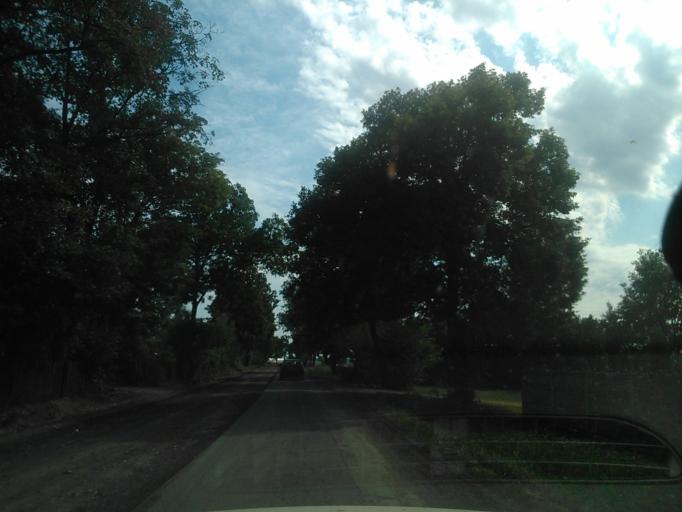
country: PL
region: Warmian-Masurian Voivodeship
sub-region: Powiat dzialdowski
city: Ilowo -Osada
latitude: 53.1980
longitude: 20.2506
